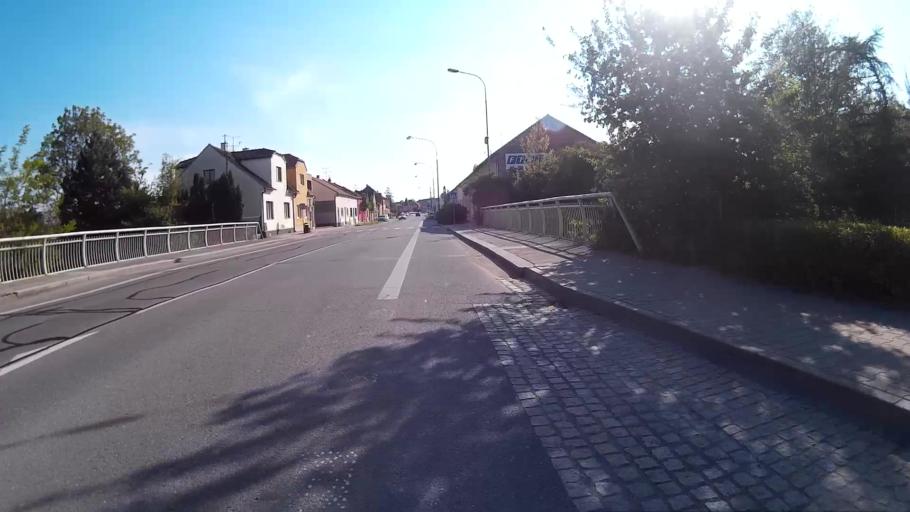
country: CZ
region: South Moravian
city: Pohorelice
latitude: 48.9846
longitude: 16.5297
